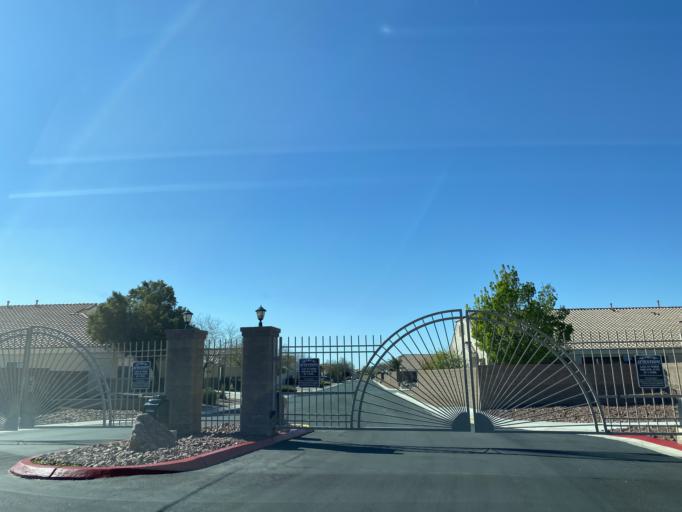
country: US
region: Nevada
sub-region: Clark County
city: North Las Vegas
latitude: 36.3355
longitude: -115.2766
